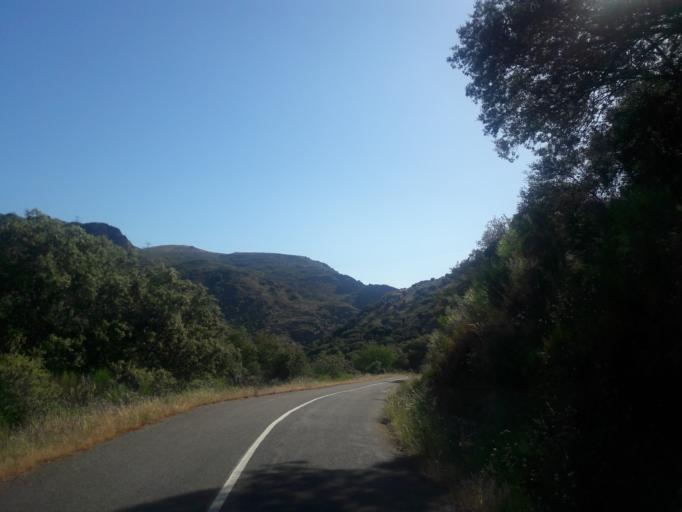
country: ES
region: Castille and Leon
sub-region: Provincia de Salamanca
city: Saucelle
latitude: 41.0256
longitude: -6.7380
